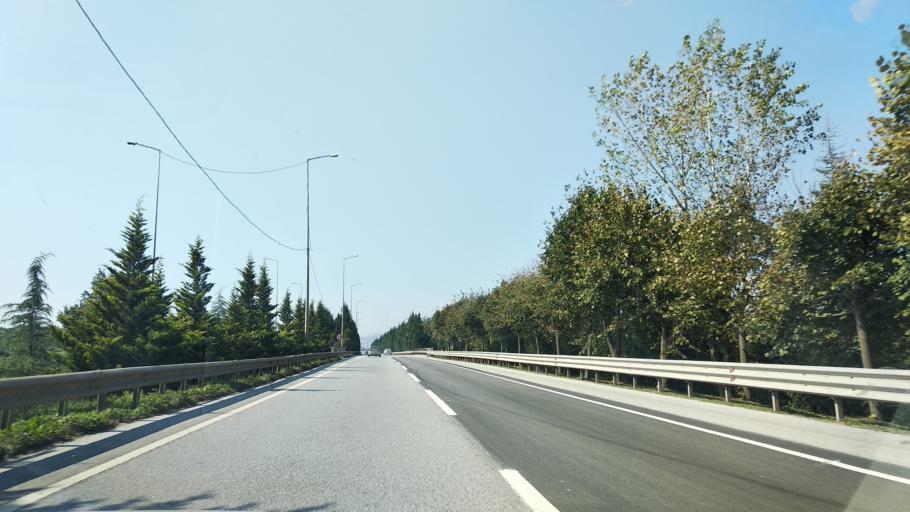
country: TR
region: Kocaeli
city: Kosekoy
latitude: 40.7554
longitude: 30.0101
